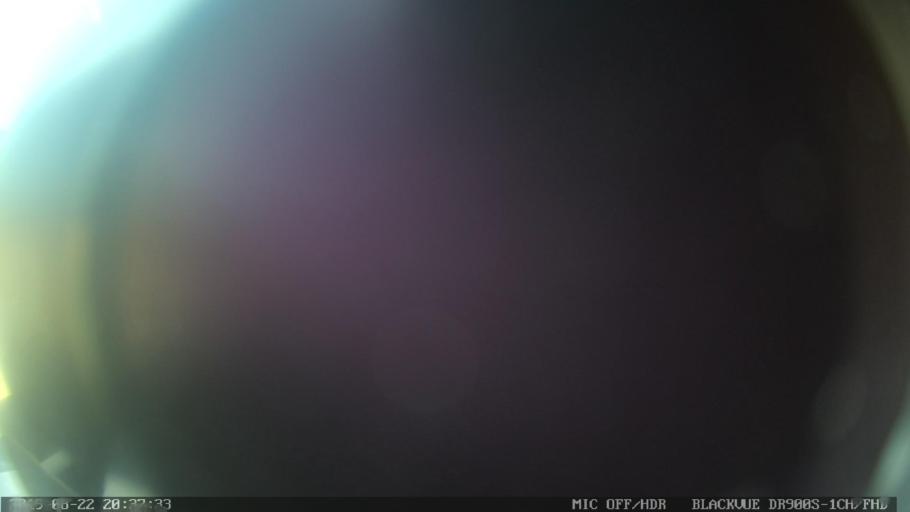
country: PT
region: Portalegre
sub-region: Nisa
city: Nisa
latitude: 39.6752
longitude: -7.7357
